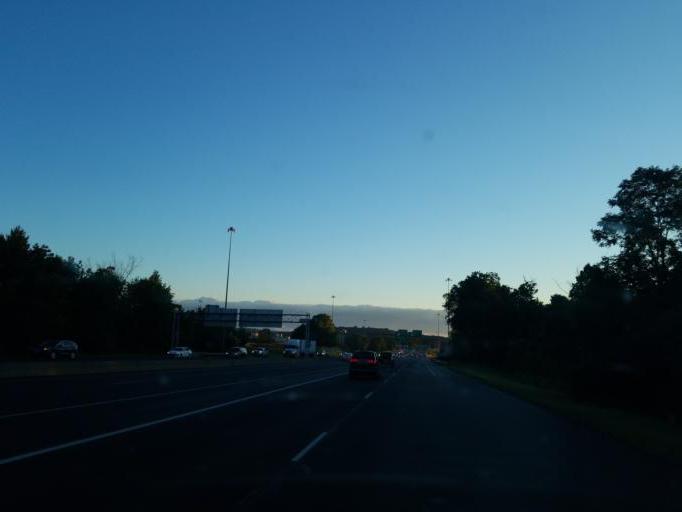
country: US
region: Ohio
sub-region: Summit County
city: Montrose-Ghent
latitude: 41.1283
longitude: -81.6523
